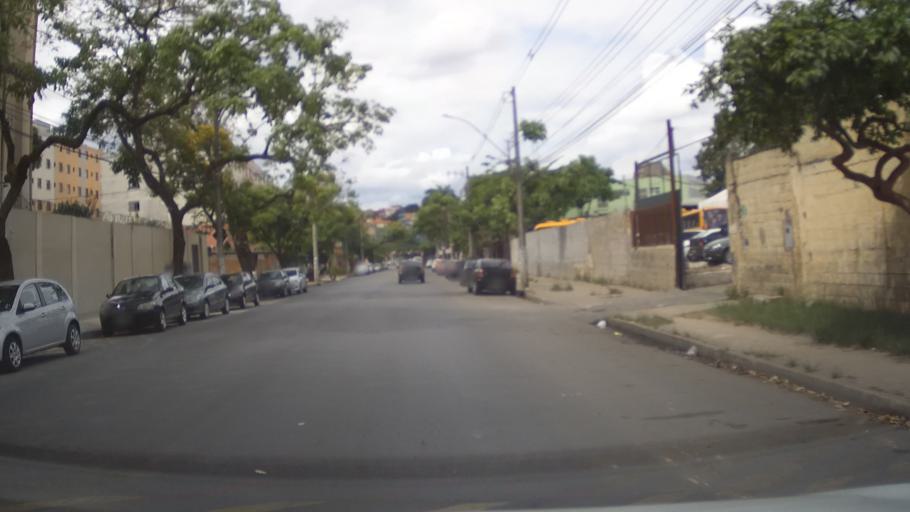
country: BR
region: Minas Gerais
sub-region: Belo Horizonte
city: Belo Horizonte
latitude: -19.8211
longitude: -43.9546
